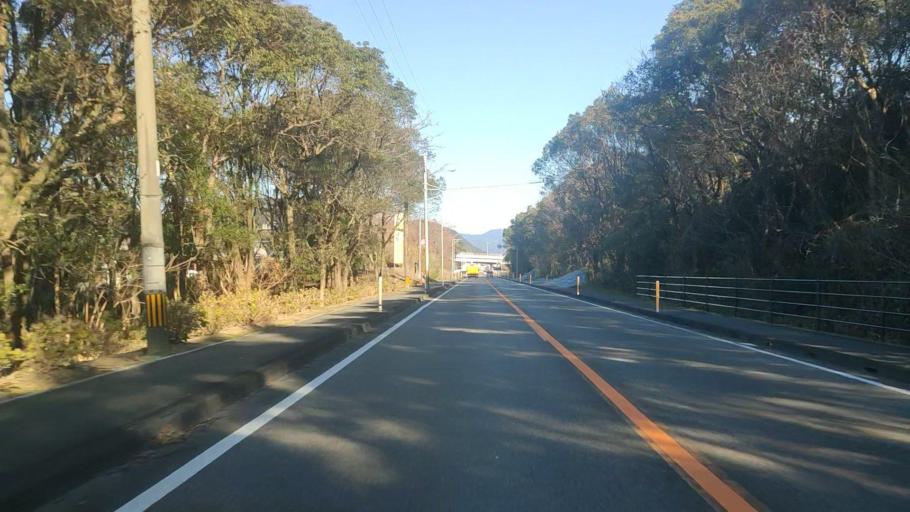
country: JP
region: Miyazaki
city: Nobeoka
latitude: 32.5330
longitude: 131.6805
